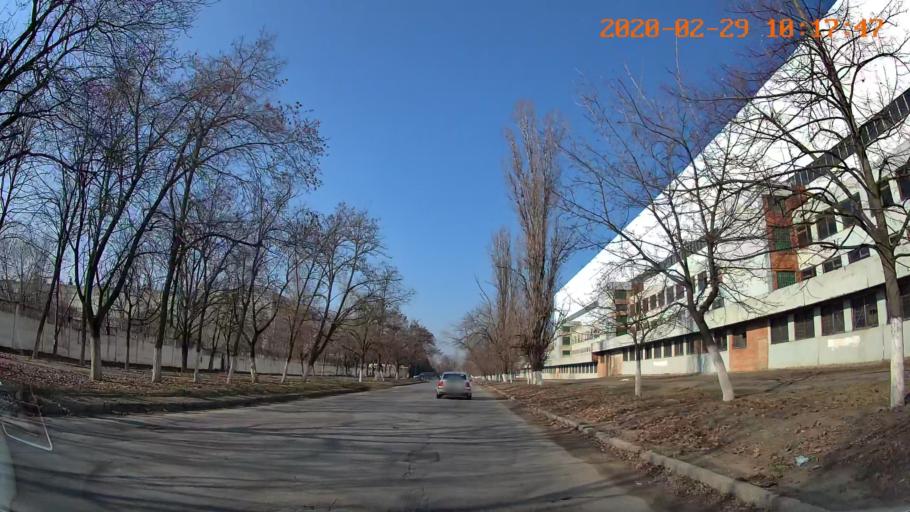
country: MD
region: Telenesti
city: Tiraspolul Nou
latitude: 46.8563
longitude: 29.6210
